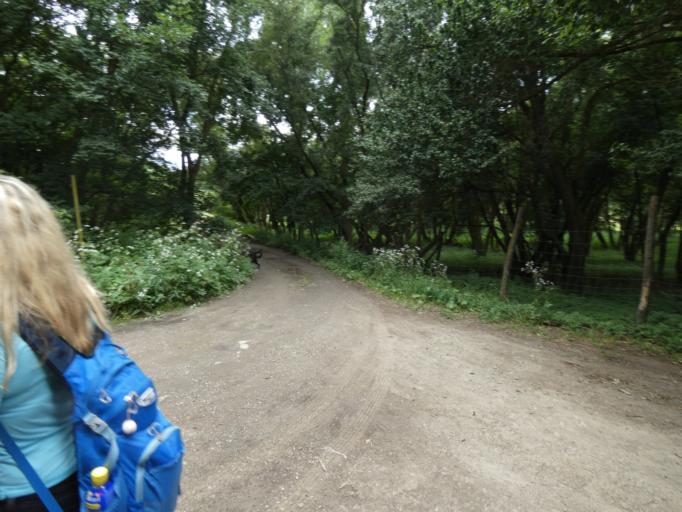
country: HU
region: Pest
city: Szob
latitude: 47.8280
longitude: 18.9010
